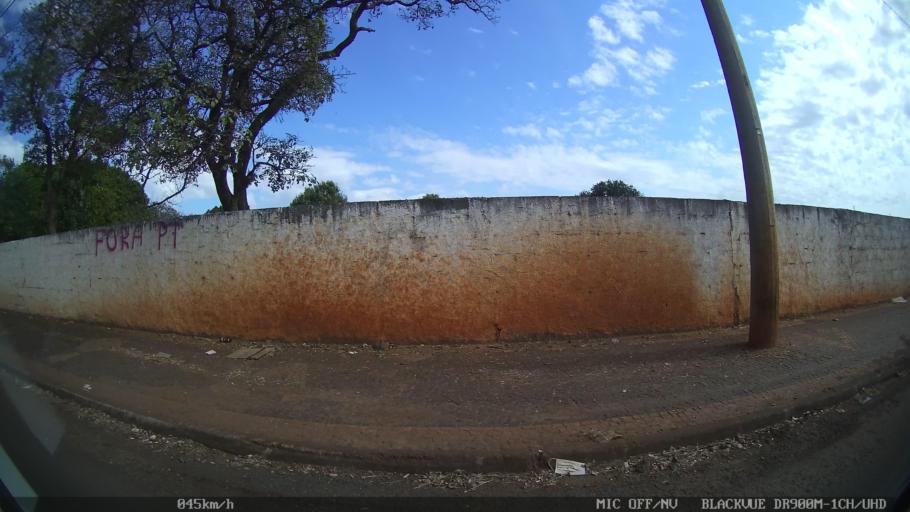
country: BR
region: Sao Paulo
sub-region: Americana
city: Americana
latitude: -22.7275
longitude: -47.3200
